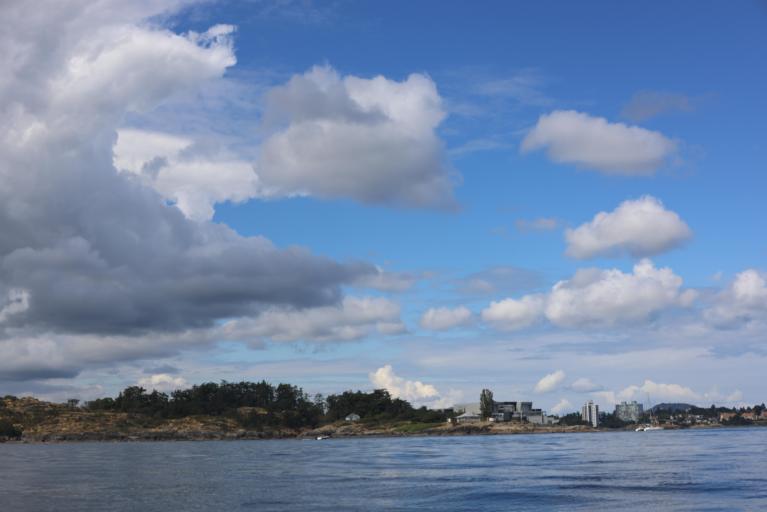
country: CA
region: British Columbia
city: Victoria
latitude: 48.4136
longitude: -123.4002
